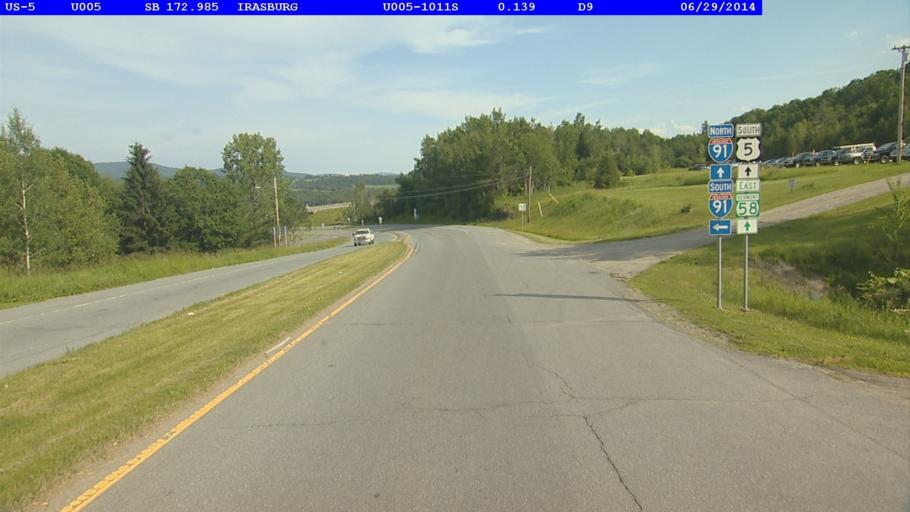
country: US
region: Vermont
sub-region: Orleans County
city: Newport
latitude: 44.8085
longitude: -72.2154
